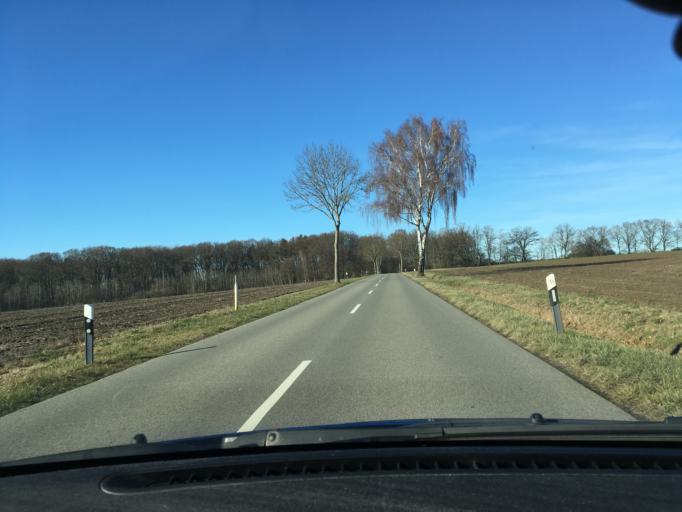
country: DE
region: Lower Saxony
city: Schwienau
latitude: 52.9715
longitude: 10.4538
